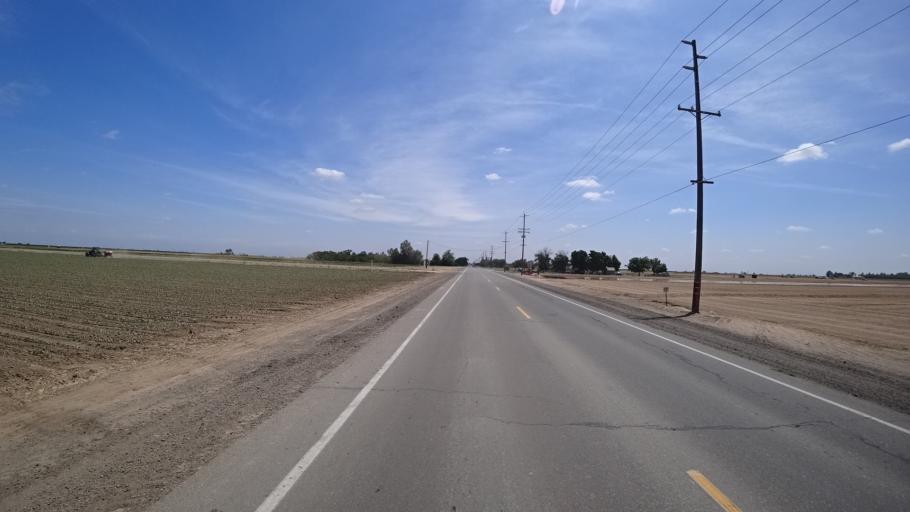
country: US
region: California
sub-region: Kings County
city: Home Garden
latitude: 36.2986
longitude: -119.5751
